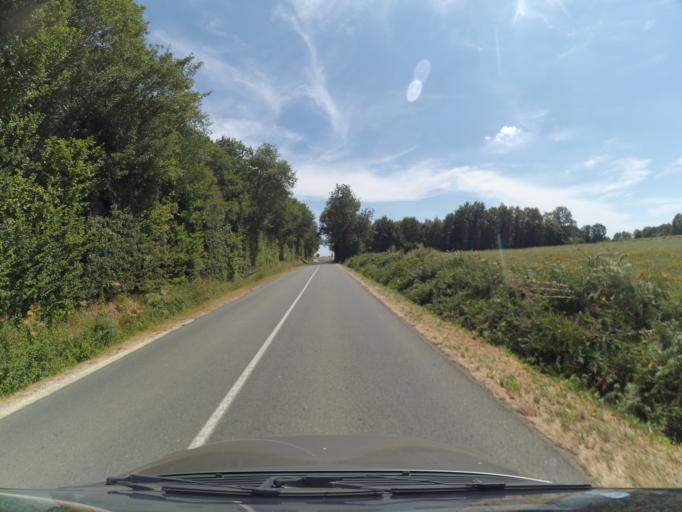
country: FR
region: Poitou-Charentes
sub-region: Departement de la Vienne
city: Saint-Maurice-la-Clouere
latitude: 46.3499
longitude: 0.4504
